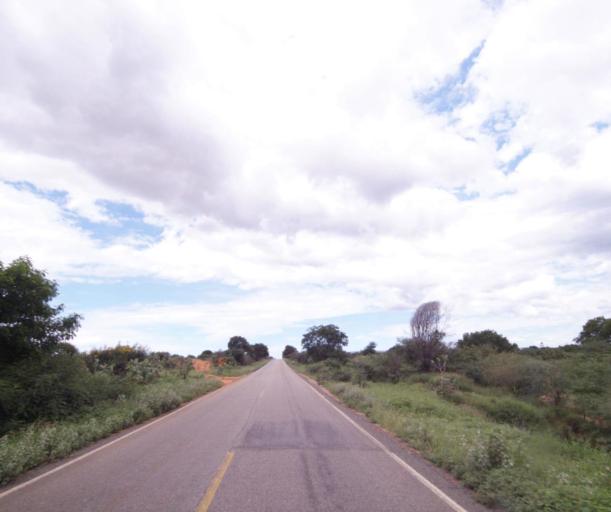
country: BR
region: Bahia
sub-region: Palmas De Monte Alto
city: Palmas de Monte Alto
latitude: -14.2598
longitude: -43.2896
